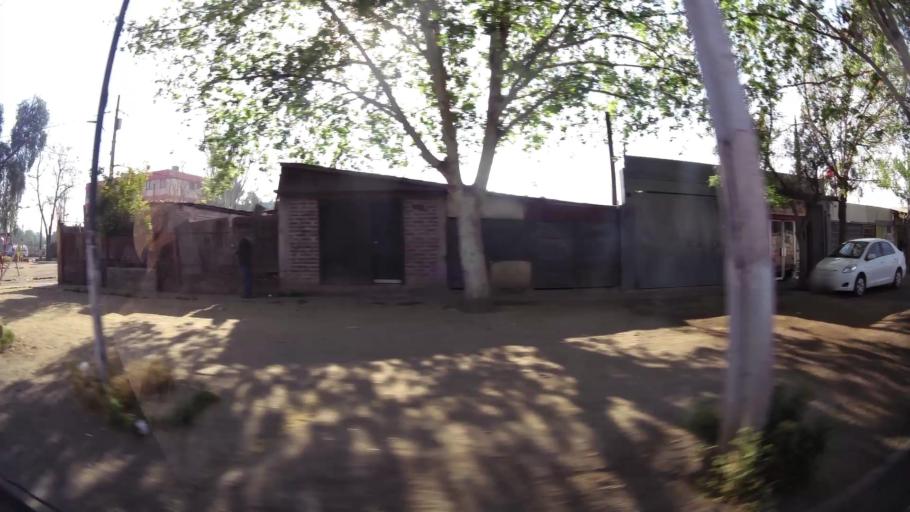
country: CL
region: Santiago Metropolitan
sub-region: Provincia de Santiago
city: Lo Prado
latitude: -33.4138
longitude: -70.7425
